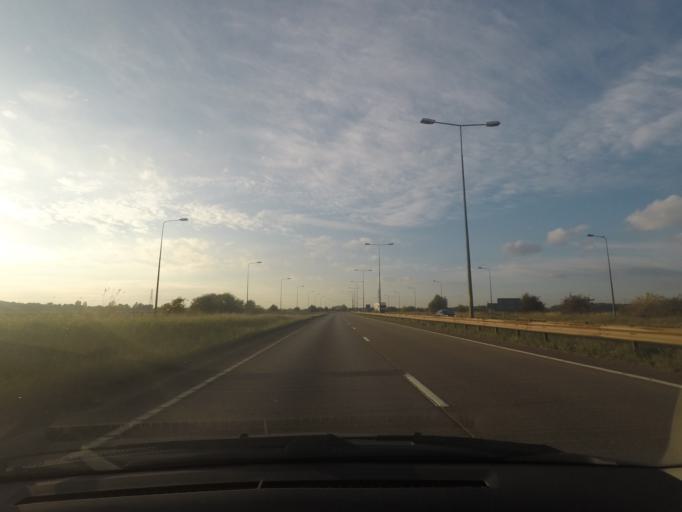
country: GB
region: England
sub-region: North East Lincolnshire
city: Great Coates
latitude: 53.5833
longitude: -0.1416
